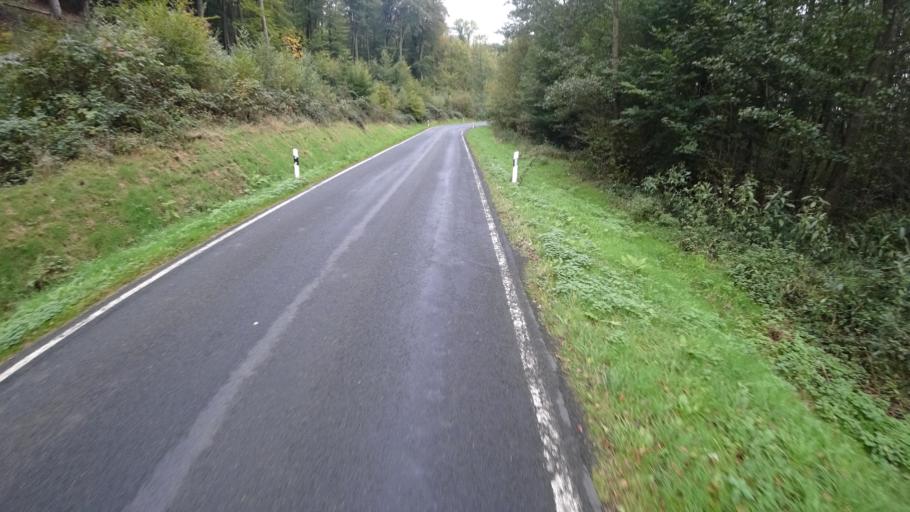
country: DE
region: Rheinland-Pfalz
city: Oberhaid
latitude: 50.5125
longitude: 7.7273
